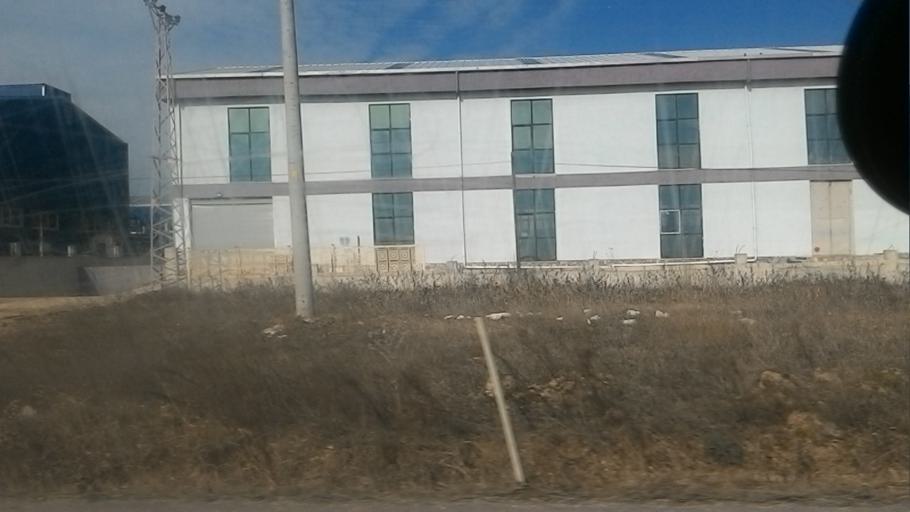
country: TR
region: Istanbul
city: Canta
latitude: 41.0794
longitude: 28.0624
